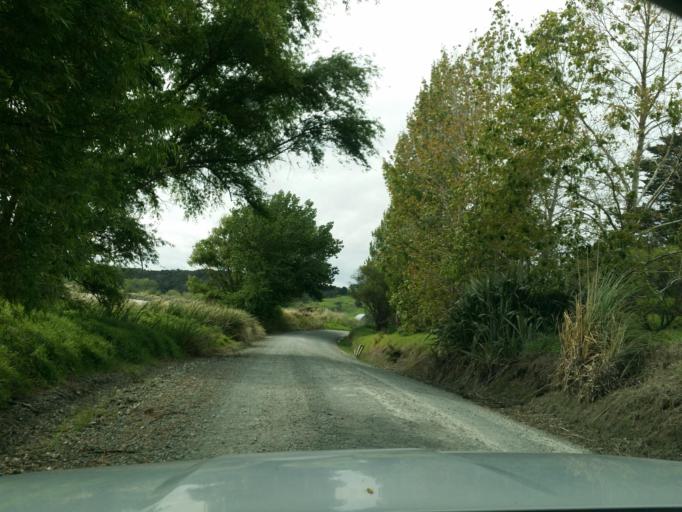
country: NZ
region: Northland
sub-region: Kaipara District
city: Dargaville
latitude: -35.9076
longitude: 173.9226
